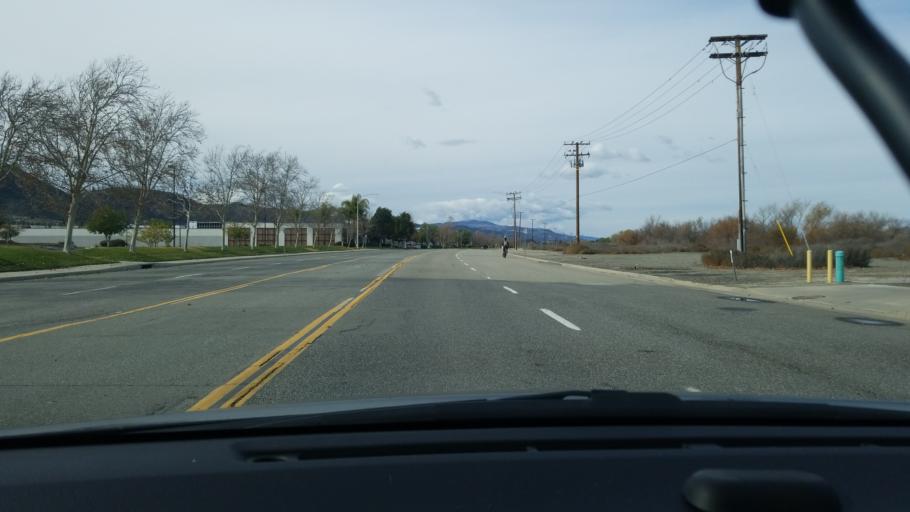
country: US
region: California
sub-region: Riverside County
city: Temecula
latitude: 33.5160
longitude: -117.1726
